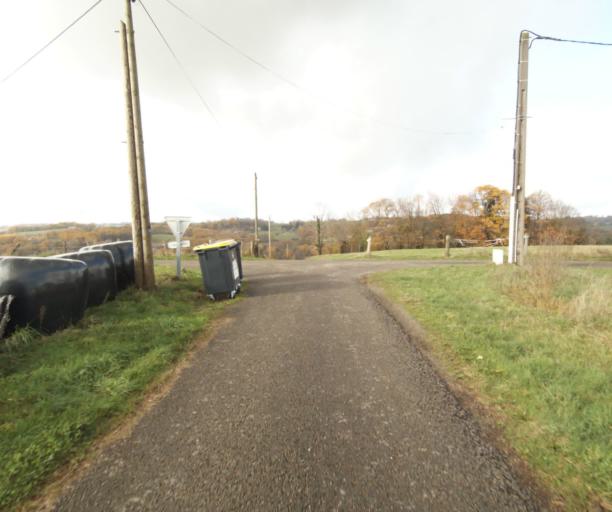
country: FR
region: Limousin
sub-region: Departement de la Correze
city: Cornil
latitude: 45.2177
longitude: 1.6418
